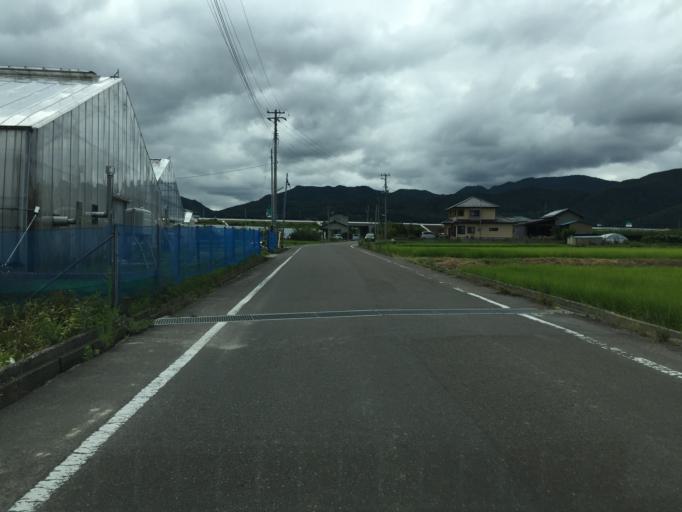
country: JP
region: Fukushima
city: Fukushima-shi
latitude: 37.7923
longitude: 140.4168
